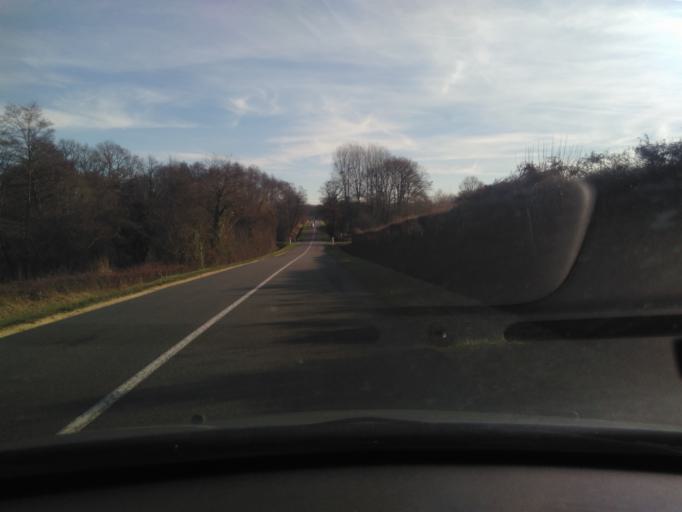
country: FR
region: Centre
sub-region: Departement du Cher
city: Chateaumeillant
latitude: 46.6352
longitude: 2.2073
